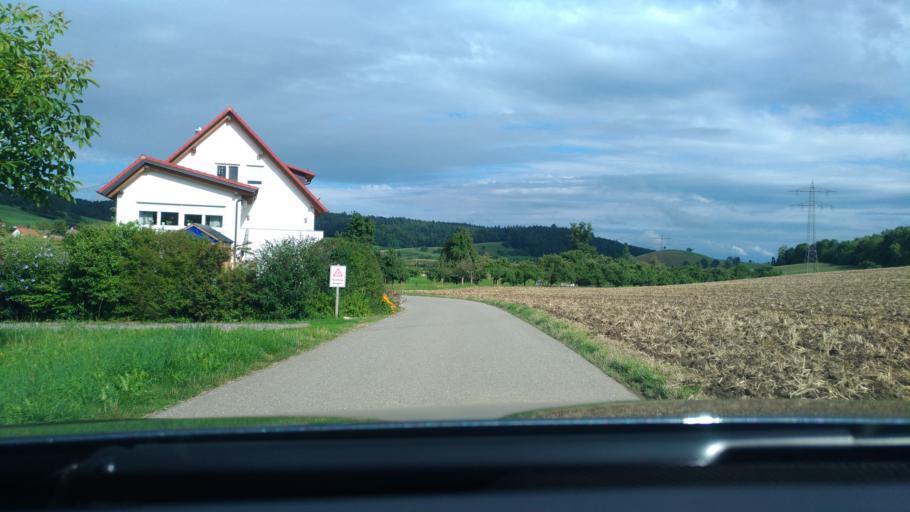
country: DE
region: Baden-Wuerttemberg
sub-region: Tuebingen Region
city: Sipplingen
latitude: 47.8165
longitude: 9.1086
